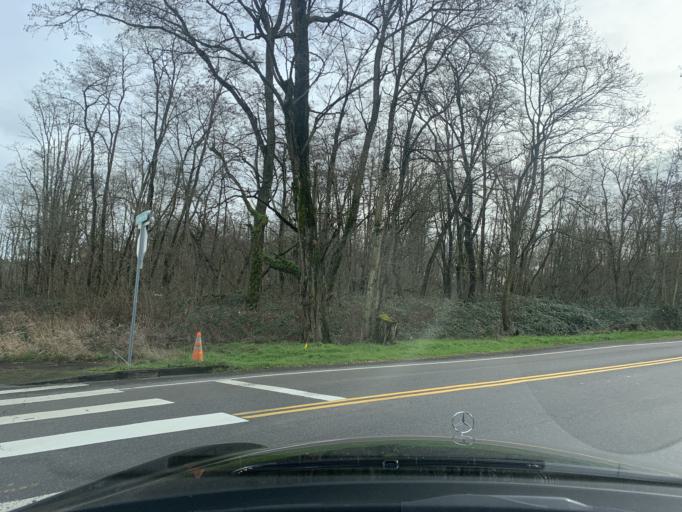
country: US
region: Oregon
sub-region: Multnomah County
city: Gresham
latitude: 45.4719
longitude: -122.4598
